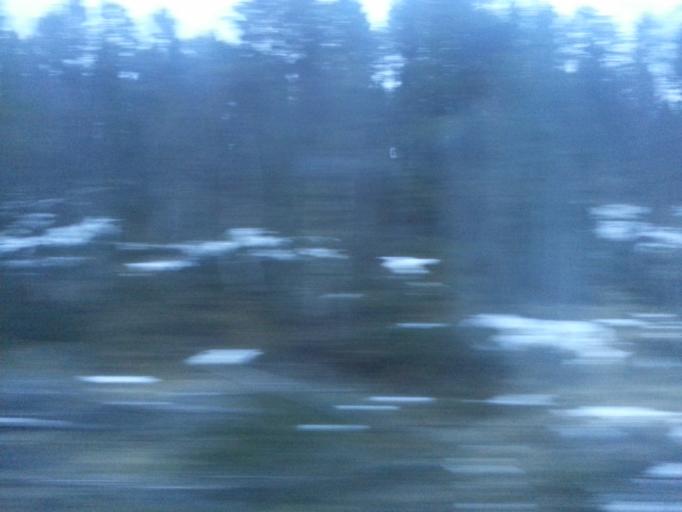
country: NO
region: Sor-Trondelag
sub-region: Rennebu
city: Berkak
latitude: 62.6986
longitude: 9.9496
